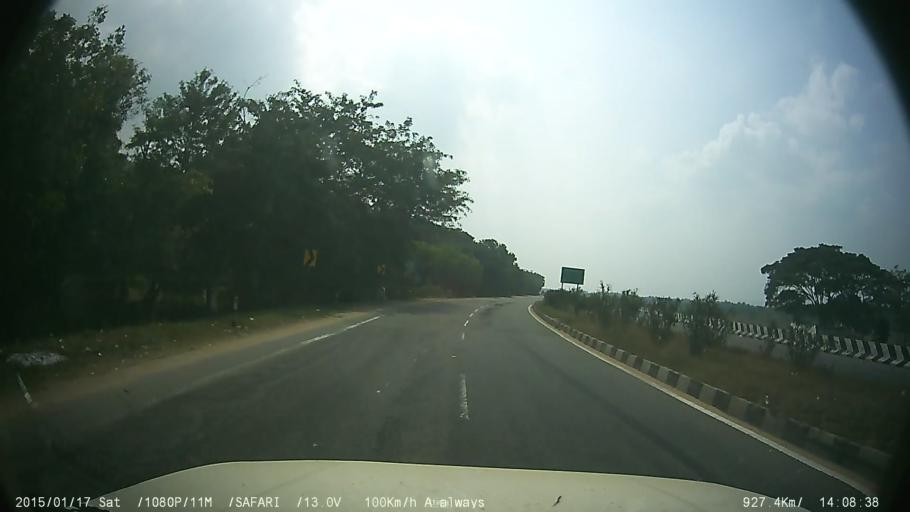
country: IN
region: Tamil Nadu
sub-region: Vellore
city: Ambur
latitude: 12.8244
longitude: 78.7594
